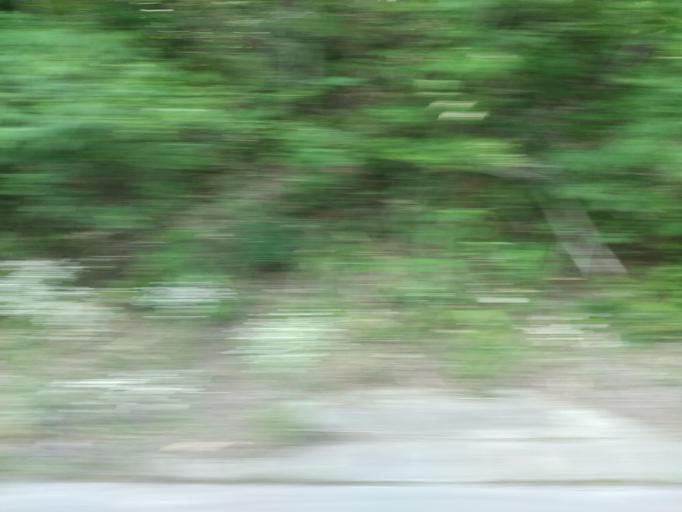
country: JP
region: Miyagi
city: Sendai
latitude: 38.2465
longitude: 140.7387
